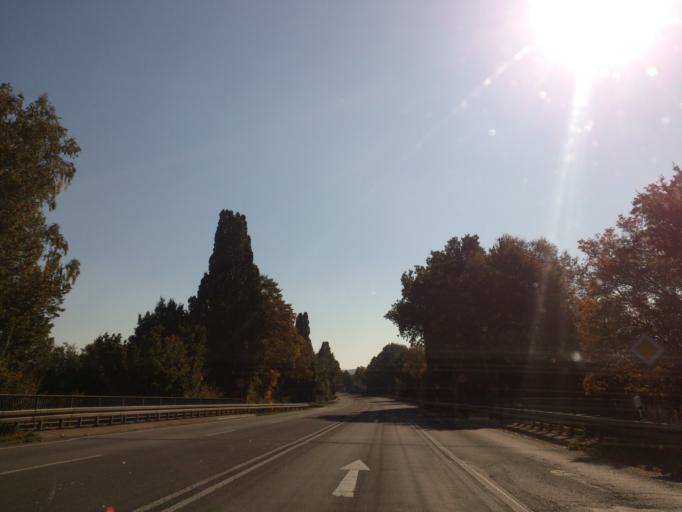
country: DE
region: Hesse
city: Liebenau
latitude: 51.4403
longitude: 9.2983
